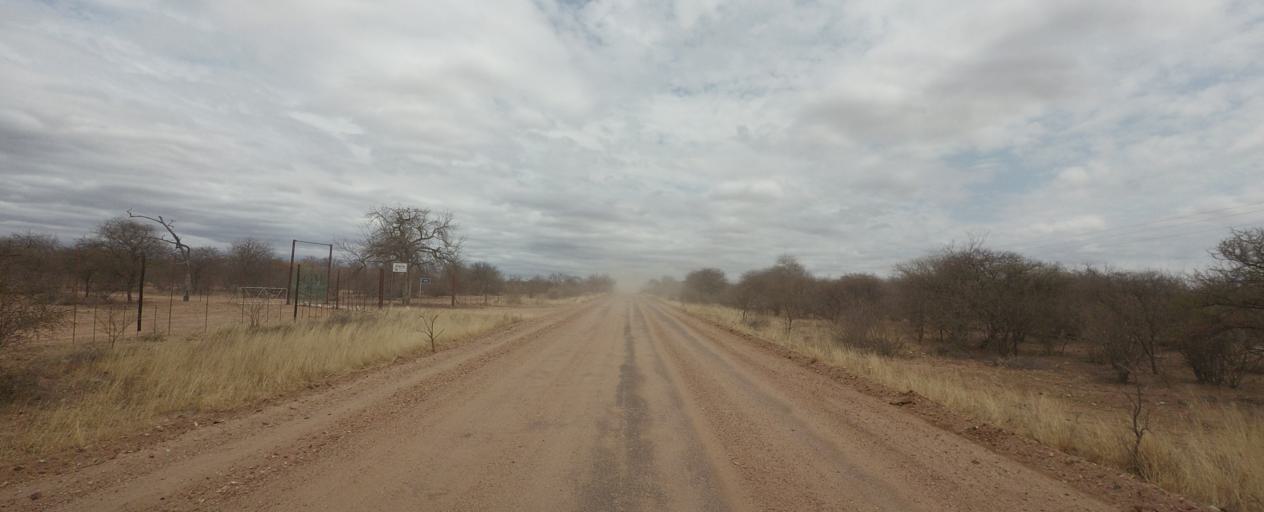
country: BW
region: Central
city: Mathathane
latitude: -22.6763
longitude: 28.6701
